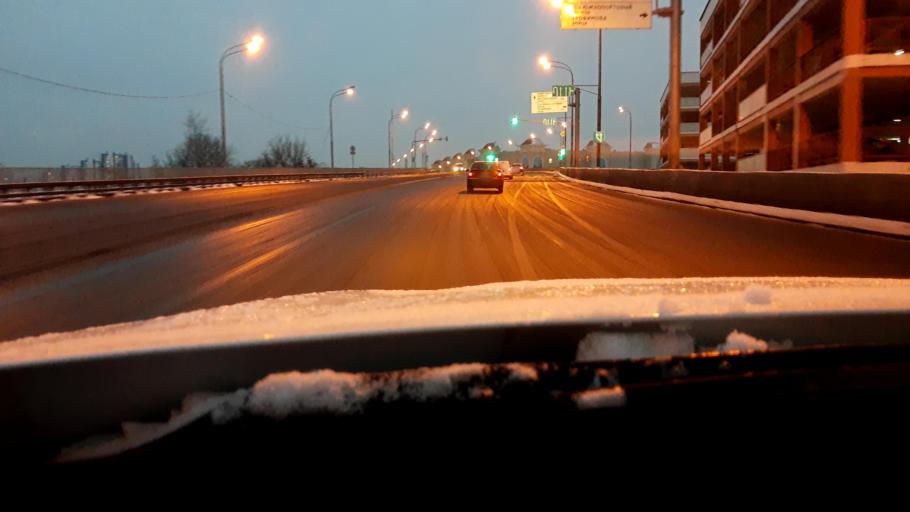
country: RU
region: Moskovskaya
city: Kozhukhovo
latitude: 55.6999
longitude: 37.6932
